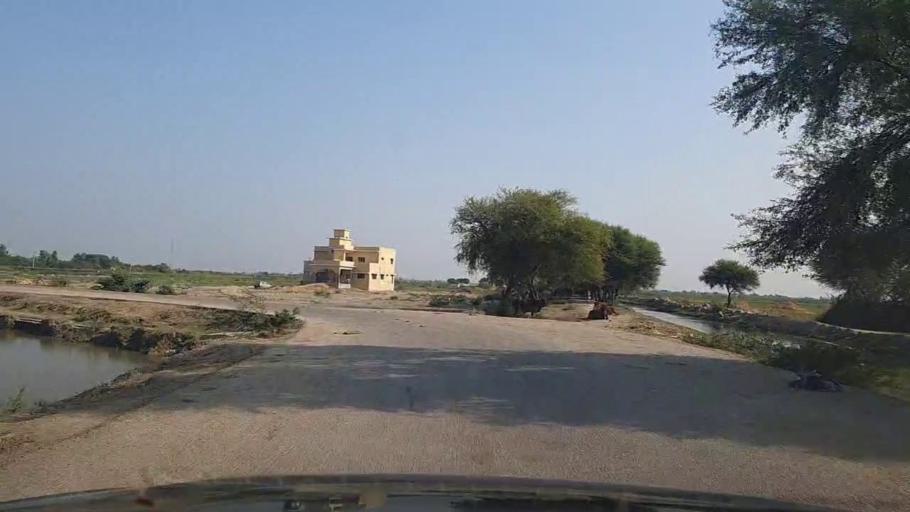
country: PK
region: Sindh
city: Chuhar Jamali
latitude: 24.5886
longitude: 68.0816
